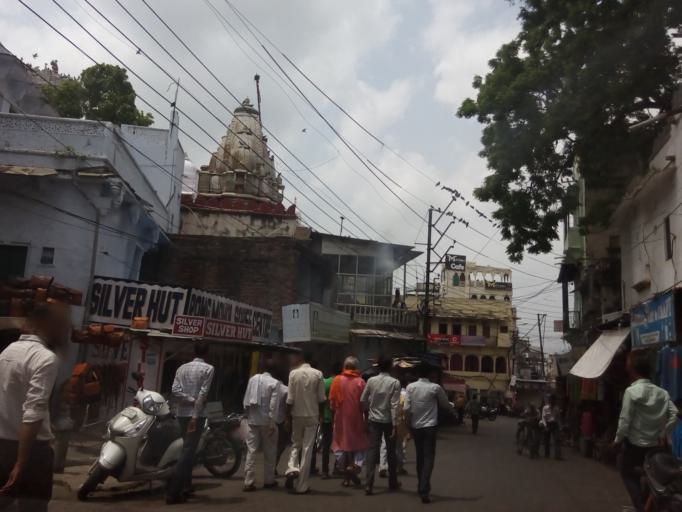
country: IN
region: Rajasthan
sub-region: Udaipur
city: Udaipur
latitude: 24.5793
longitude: 73.6839
